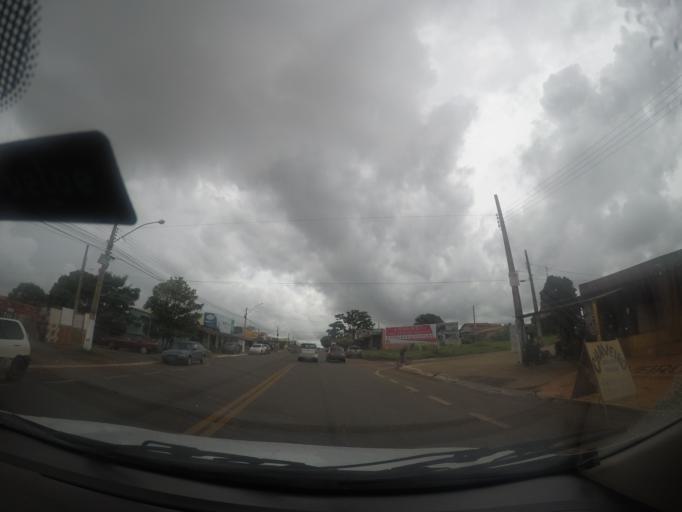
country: BR
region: Goias
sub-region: Trindade
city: Trindade
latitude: -16.6375
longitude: -49.3903
